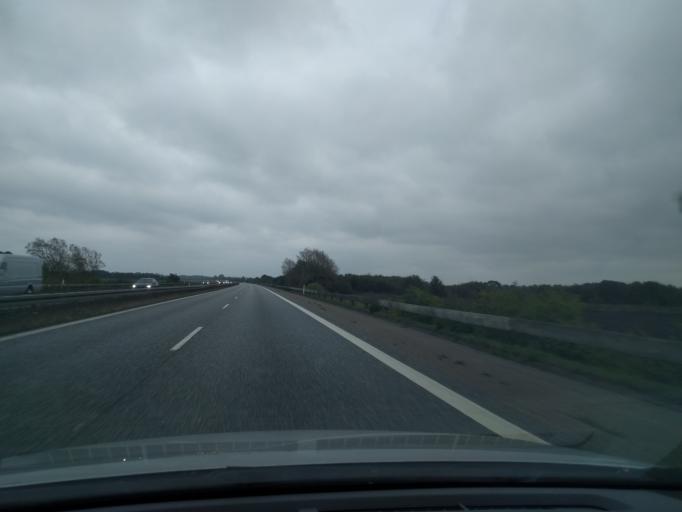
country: DK
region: Zealand
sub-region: Soro Kommune
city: Frederiksberg
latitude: 55.4483
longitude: 11.6569
